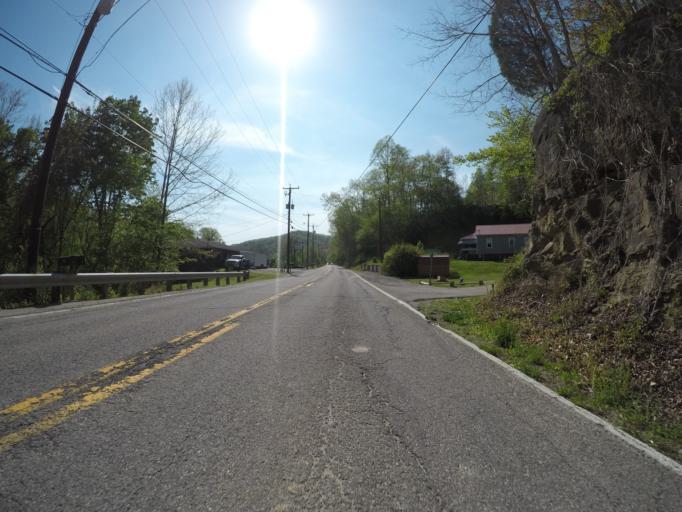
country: US
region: West Virginia
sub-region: Kanawha County
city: Clendenin
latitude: 38.4751
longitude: -81.3870
